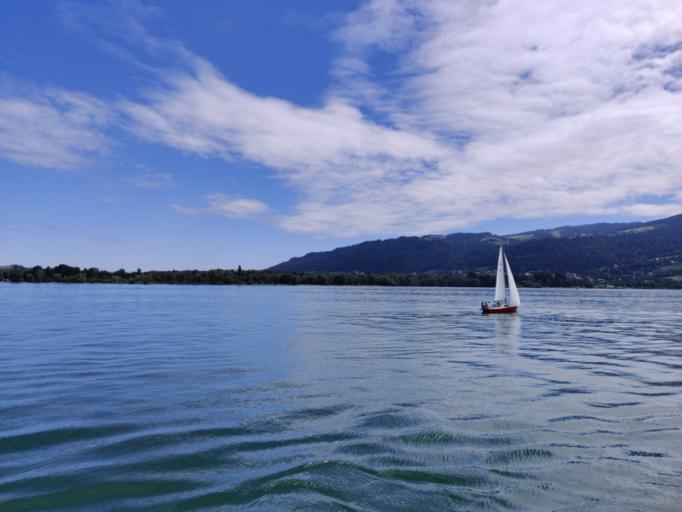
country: AT
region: Vorarlberg
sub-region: Politischer Bezirk Bregenz
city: Lochau
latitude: 47.5262
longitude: 9.7243
